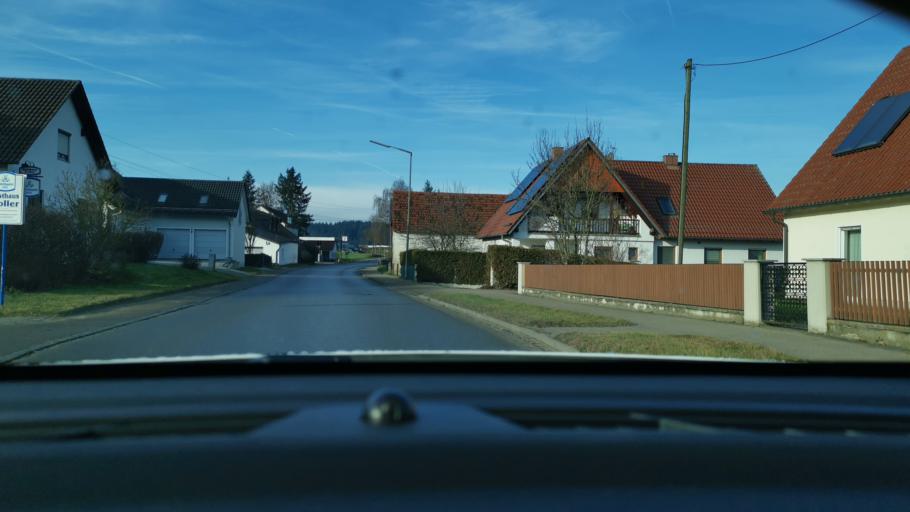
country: DE
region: Bavaria
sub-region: Swabia
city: Hollenbach
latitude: 48.5042
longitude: 11.0586
